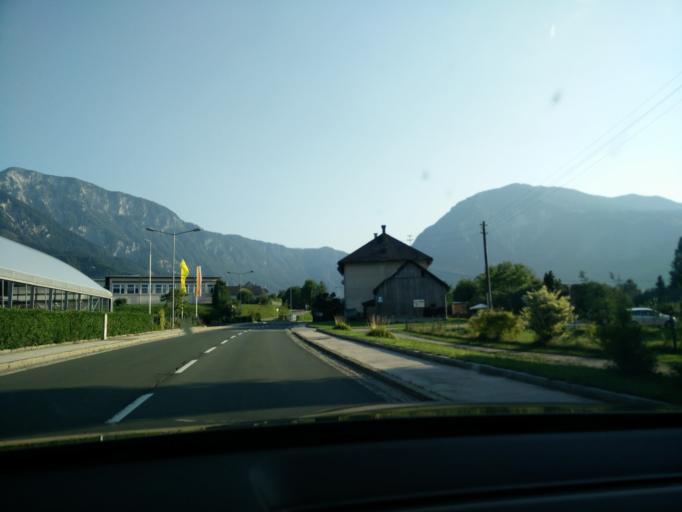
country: AT
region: Carinthia
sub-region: Politischer Bezirk Klagenfurt Land
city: Ferlach
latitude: 46.5329
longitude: 14.3040
